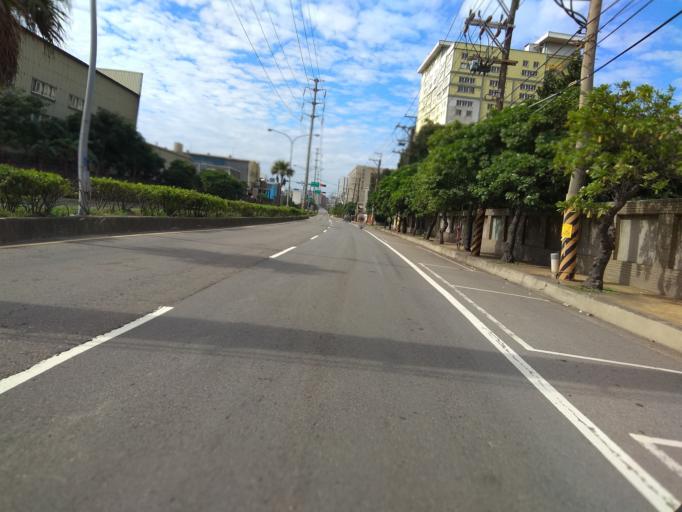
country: TW
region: Taiwan
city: Taoyuan City
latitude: 25.0554
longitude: 121.1313
